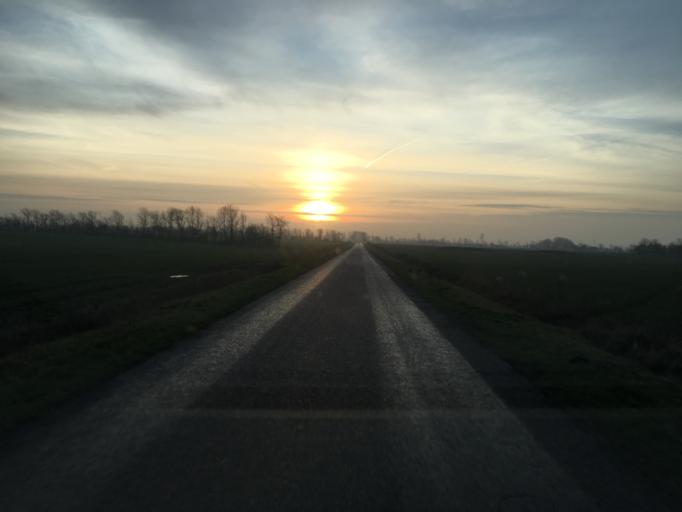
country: DK
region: South Denmark
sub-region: Tonder Kommune
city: Logumkloster
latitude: 55.1156
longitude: 9.0215
